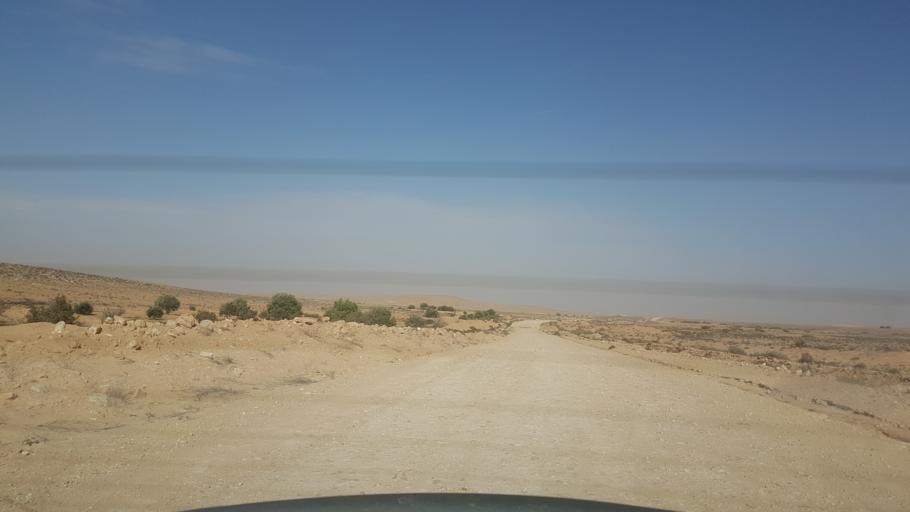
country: TN
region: Qabis
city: El Hamma
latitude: 33.6614
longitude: 9.7348
